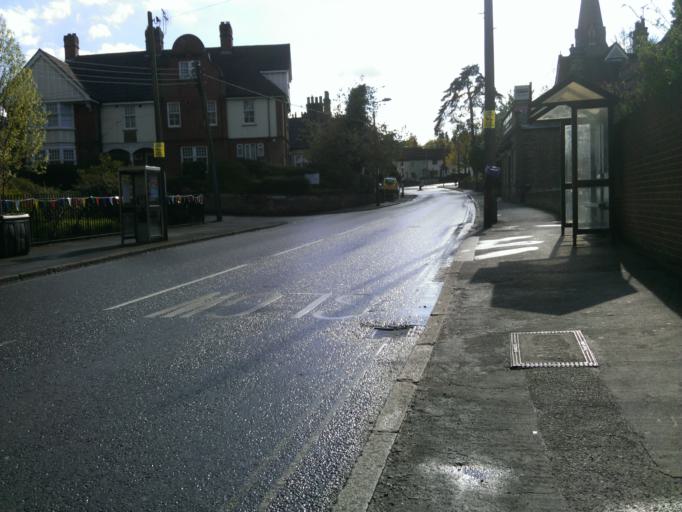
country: GB
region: England
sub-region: Essex
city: Sible Hedingham
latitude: 51.9436
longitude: 0.6316
